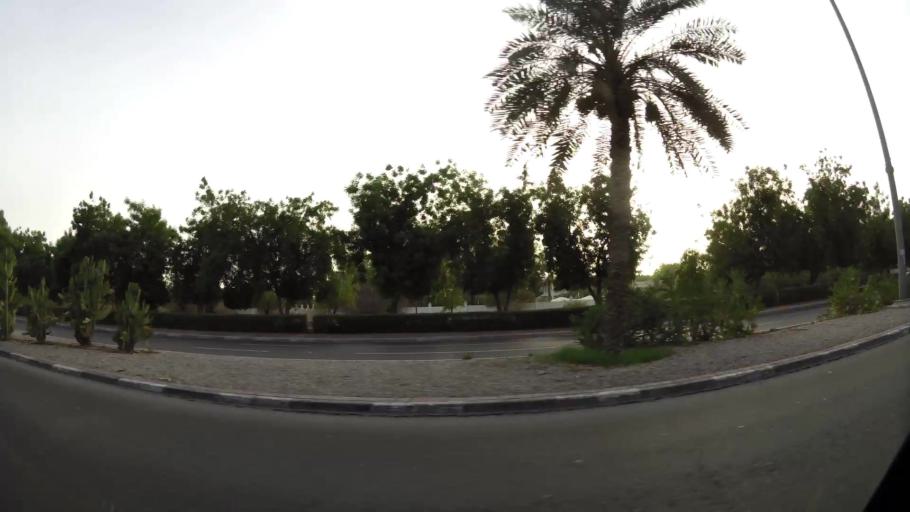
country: AE
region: Abu Dhabi
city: Al Ain
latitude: 24.2516
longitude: 55.7199
